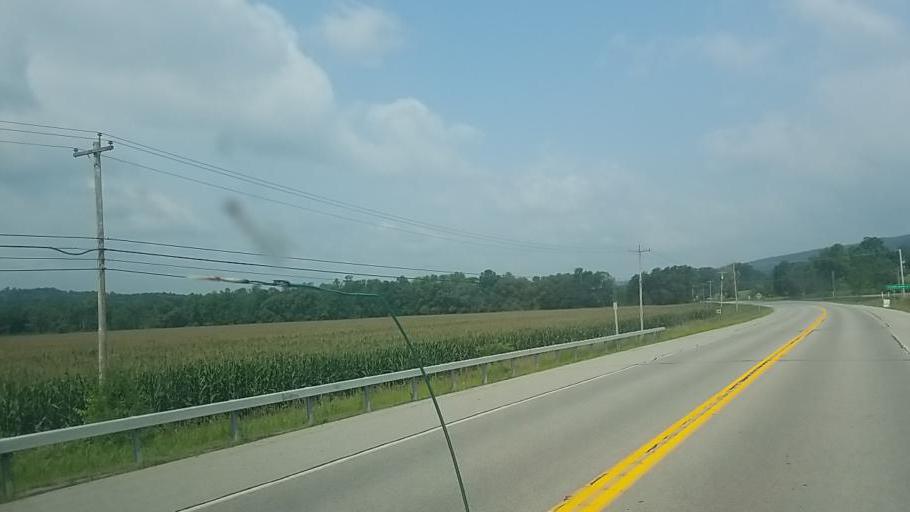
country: US
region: New York
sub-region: Montgomery County
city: Fort Plain
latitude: 42.9688
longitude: -74.6290
